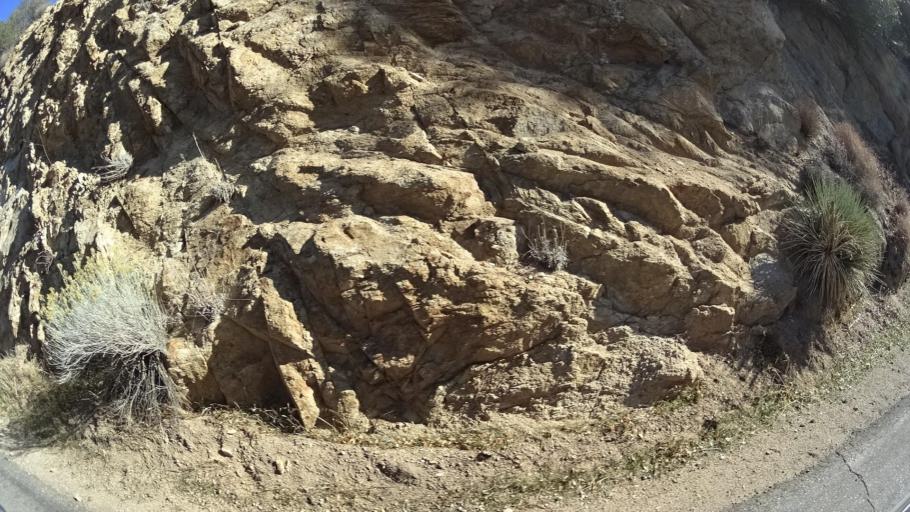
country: US
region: California
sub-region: Kern County
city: Bodfish
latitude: 35.5748
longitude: -118.5580
